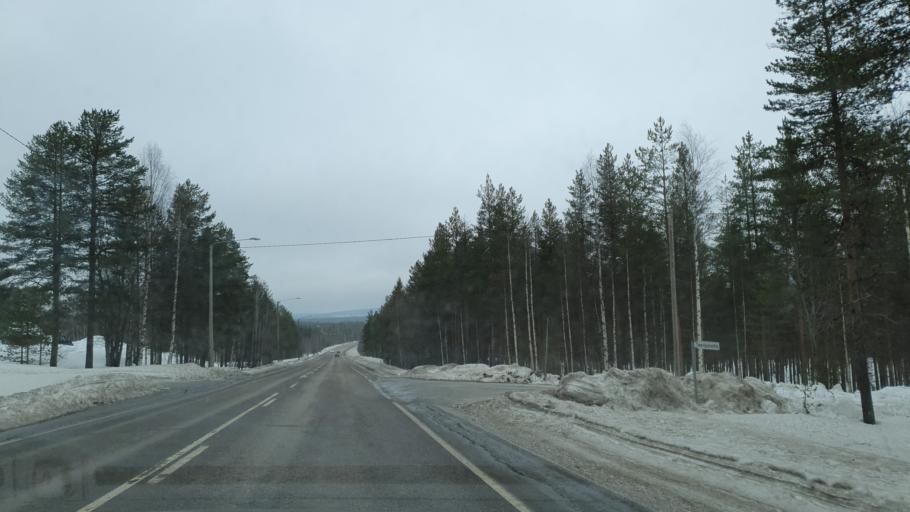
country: FI
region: Lapland
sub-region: Torniolaakso
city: Pello
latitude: 66.8955
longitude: 24.0914
